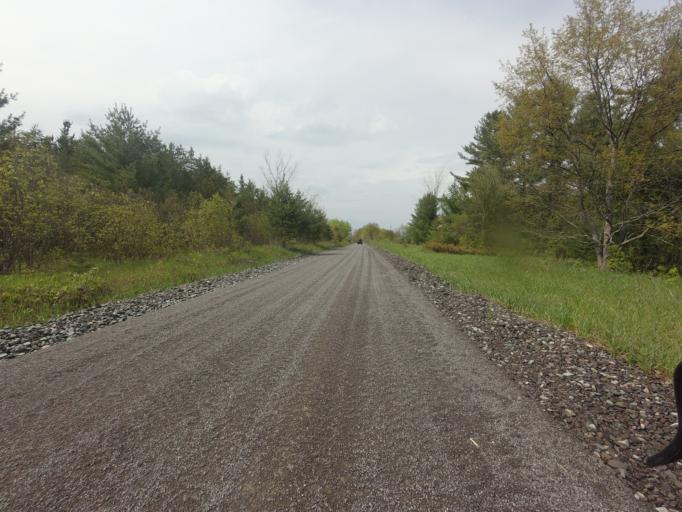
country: CA
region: Ontario
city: Carleton Place
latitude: 45.1584
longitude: -76.1451
